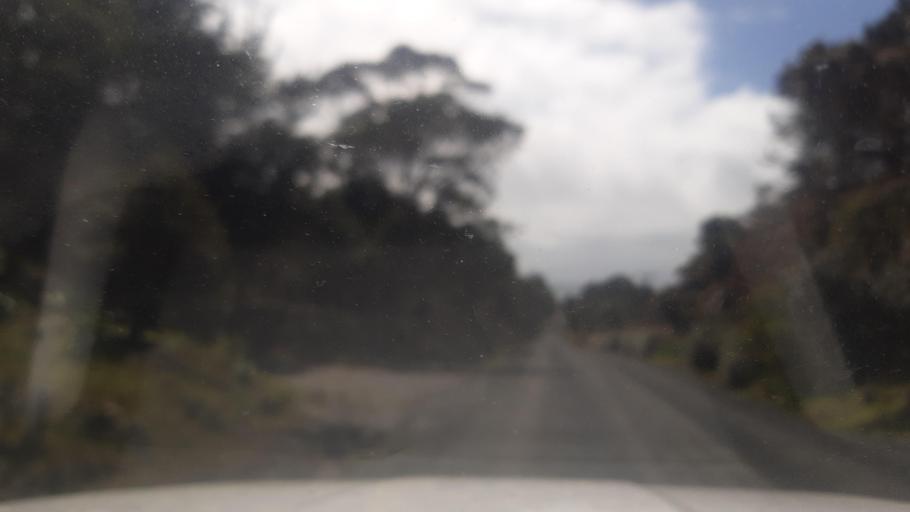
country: NZ
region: Northland
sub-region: Far North District
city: Kaitaia
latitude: -34.7437
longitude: 173.1047
